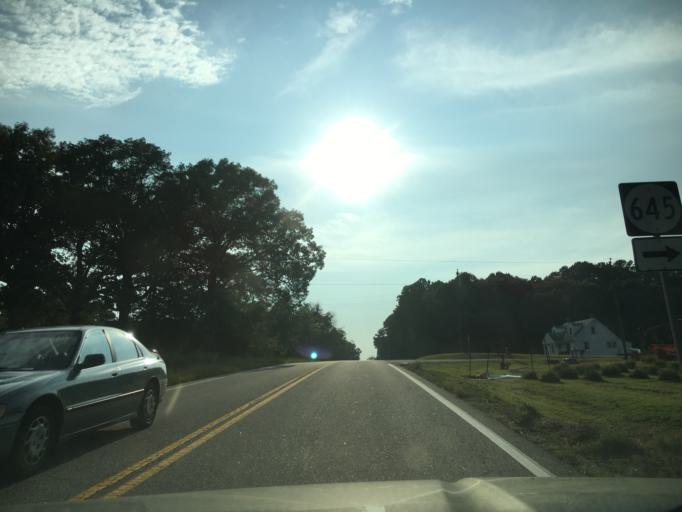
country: US
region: Virginia
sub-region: Nottoway County
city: Crewe
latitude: 37.2744
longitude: -78.1263
